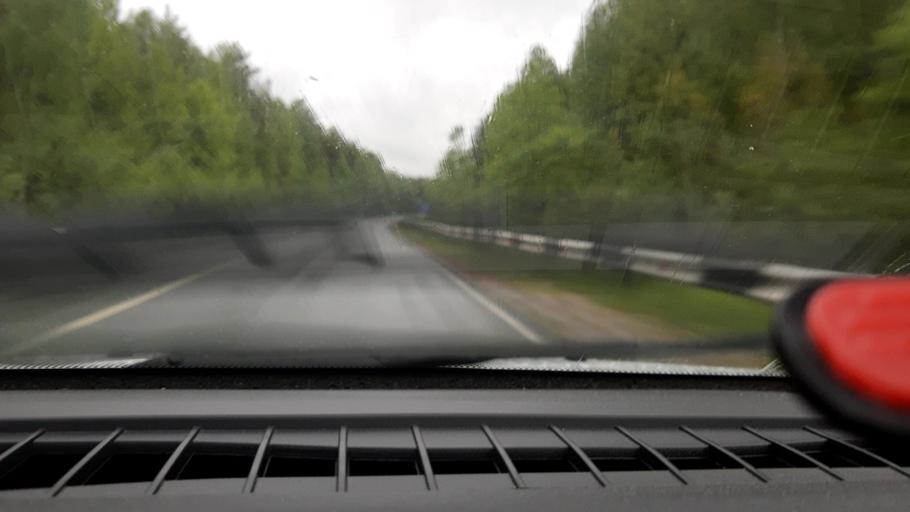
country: RU
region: Nizjnij Novgorod
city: Semenov
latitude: 56.8028
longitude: 44.4611
